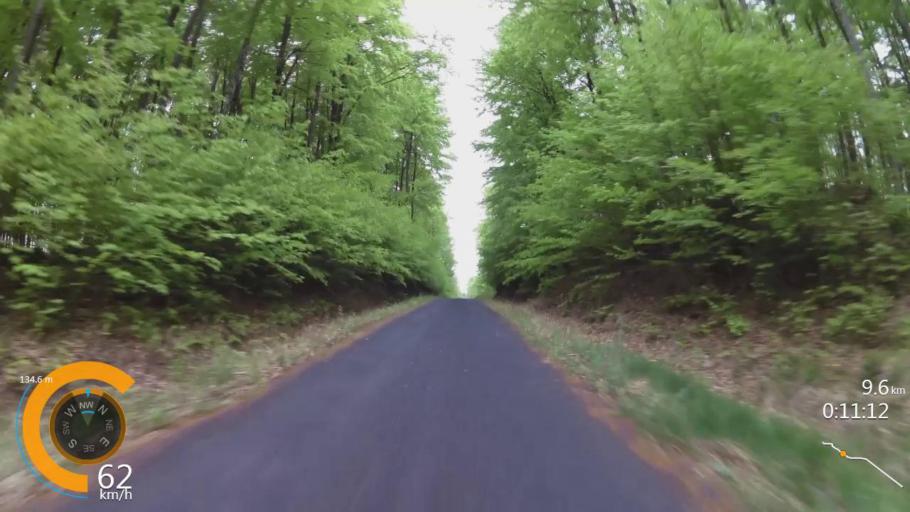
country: PL
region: West Pomeranian Voivodeship
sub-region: Powiat drawski
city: Wierzchowo
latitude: 53.5113
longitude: 16.1161
